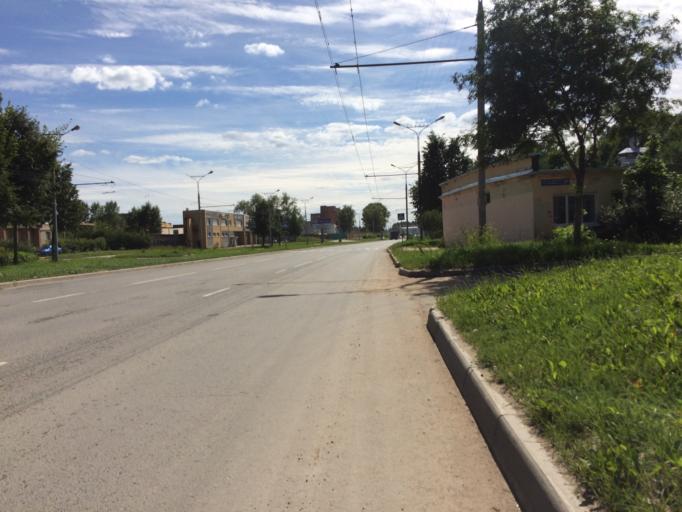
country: RU
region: Mariy-El
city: Yoshkar-Ola
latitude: 56.6312
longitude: 47.9387
